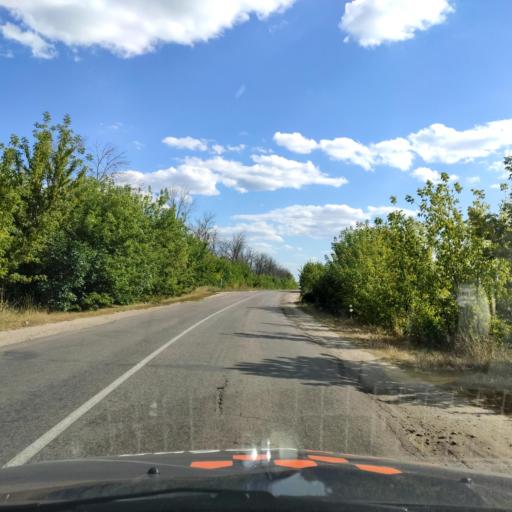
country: RU
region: Voronezj
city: Somovo
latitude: 51.7035
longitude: 39.3731
